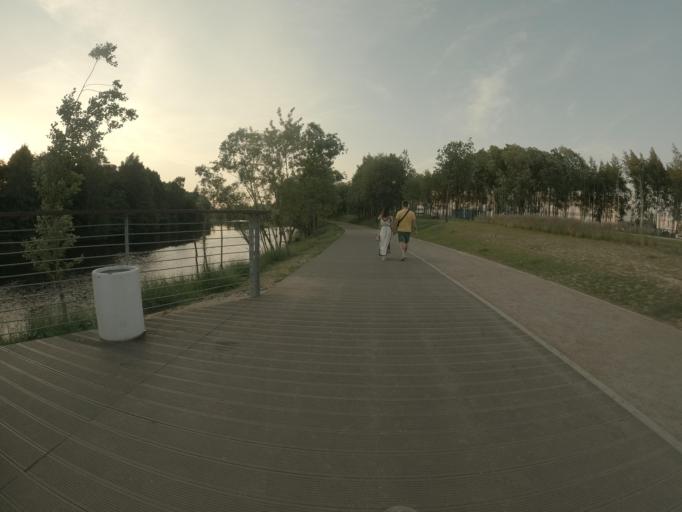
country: RU
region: St.-Petersburg
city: Krasnogvargeisky
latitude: 59.9436
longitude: 30.4567
